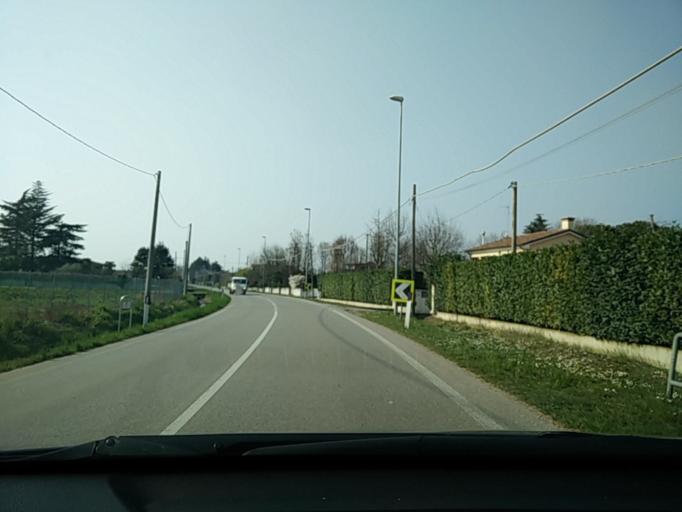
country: IT
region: Veneto
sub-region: Provincia di Treviso
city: Santandra
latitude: 45.7317
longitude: 12.1940
